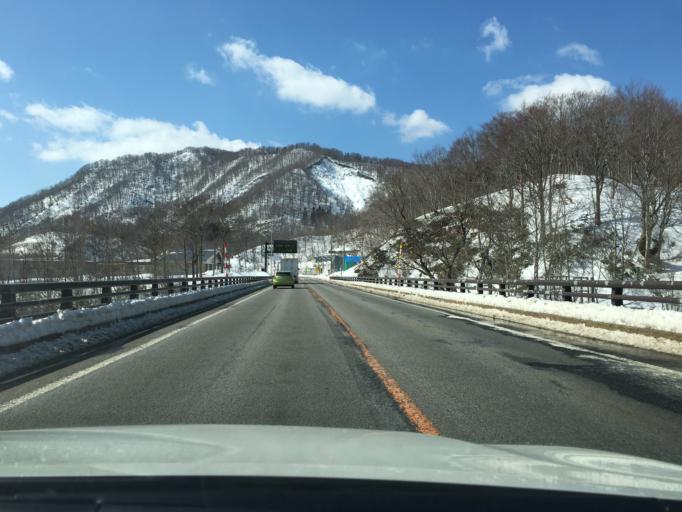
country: JP
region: Yamagata
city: Tsuruoka
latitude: 38.5801
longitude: 139.9419
